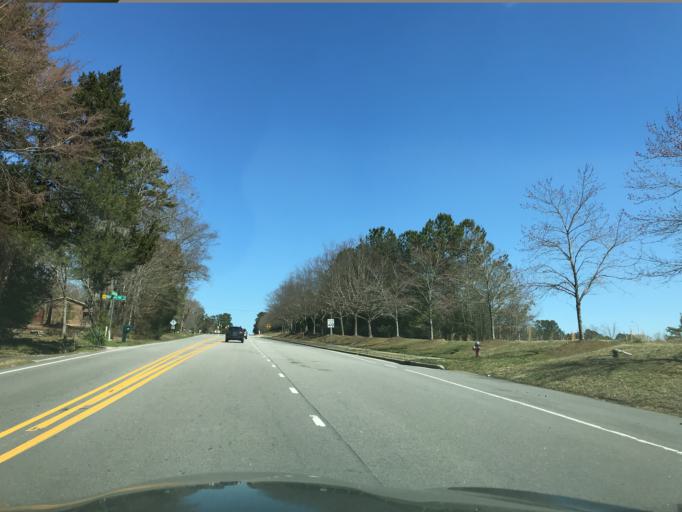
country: US
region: North Carolina
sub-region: Wake County
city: Wake Forest
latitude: 35.9479
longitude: -78.5740
